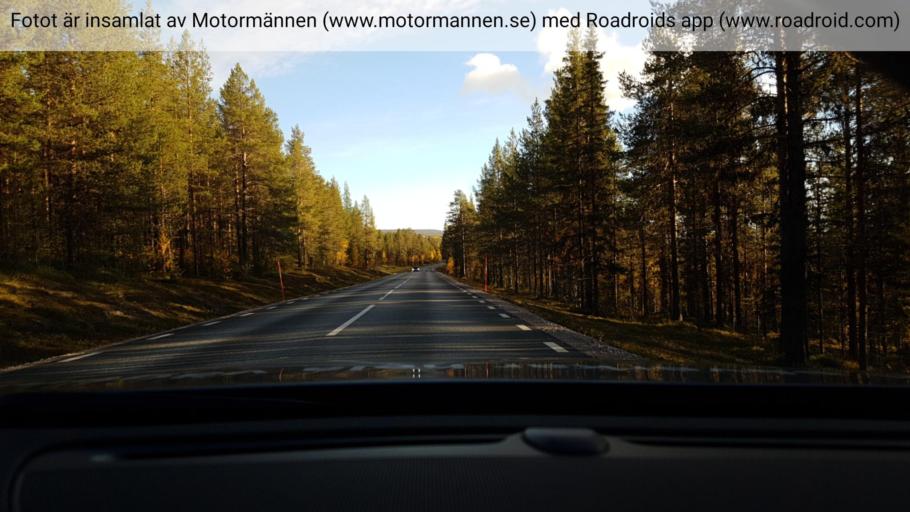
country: SE
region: Norrbotten
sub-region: Jokkmokks Kommun
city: Jokkmokk
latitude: 66.9248
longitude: 19.8257
